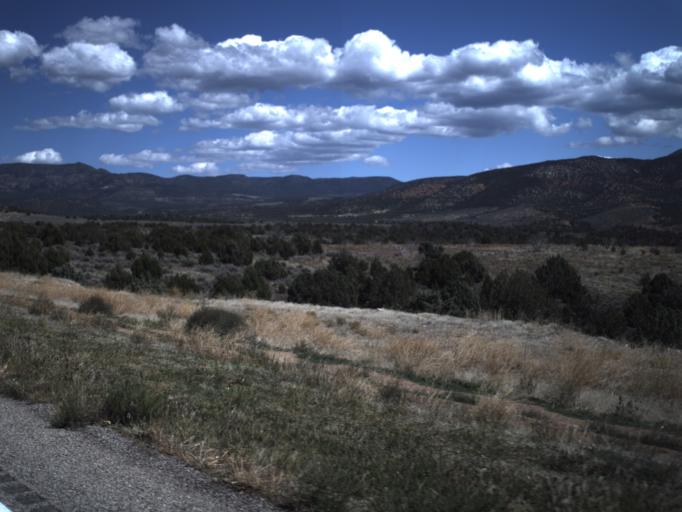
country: US
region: Utah
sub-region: Washington County
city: Enterprise
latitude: 37.3774
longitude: -113.6550
